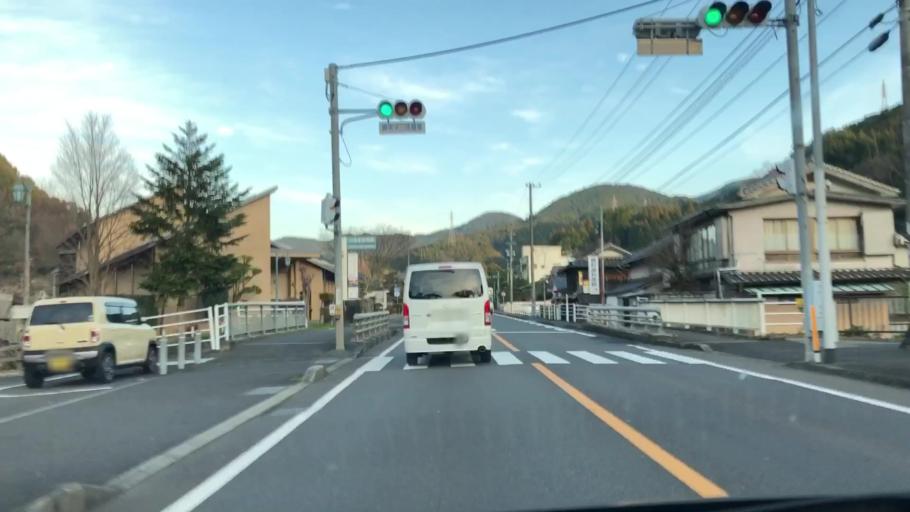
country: JP
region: Kumamoto
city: Minamata
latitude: 32.2315
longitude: 130.4572
